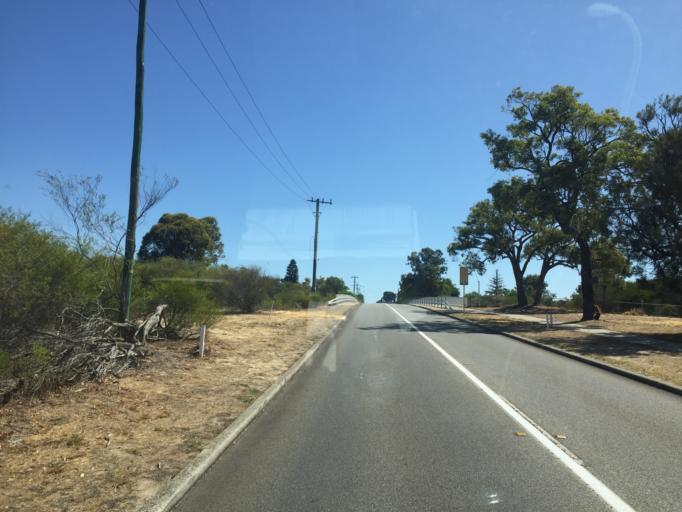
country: AU
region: Western Australia
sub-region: Belmont
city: Redcliffe
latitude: -31.9362
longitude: 115.9459
